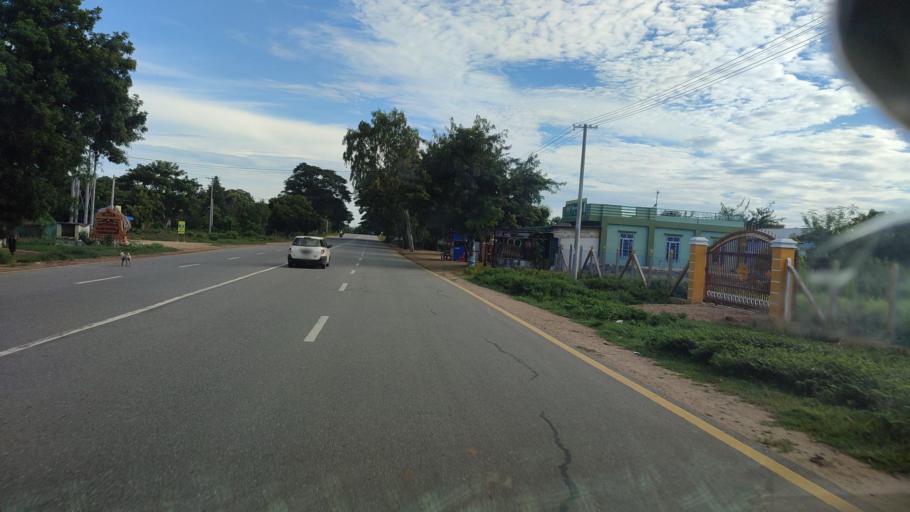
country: MM
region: Mandalay
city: Yamethin
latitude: 20.2097
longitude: 96.1812
